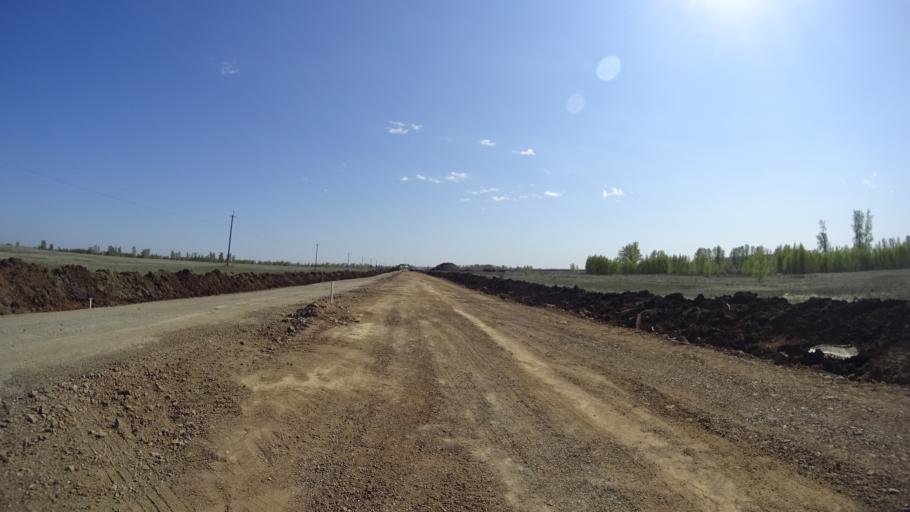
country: RU
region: Chelyabinsk
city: Troitsk
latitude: 54.1816
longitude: 61.4807
